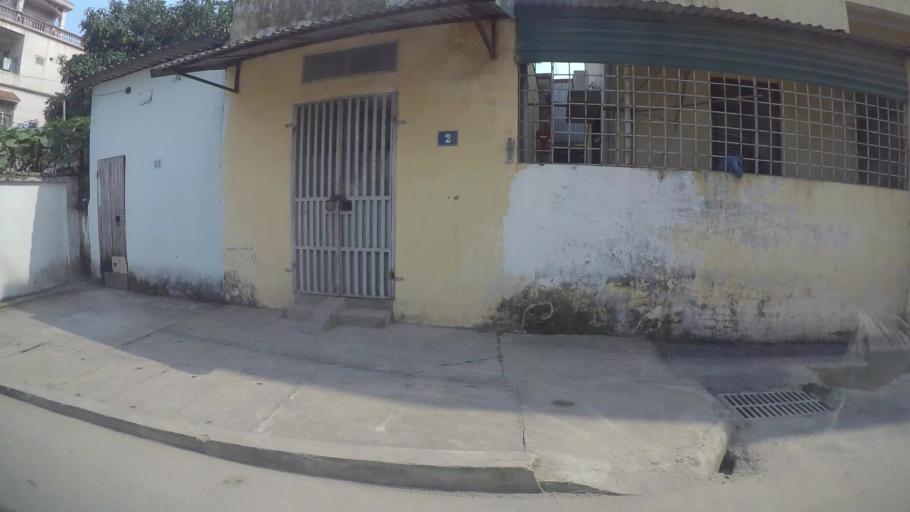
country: VN
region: Ha Noi
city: Ha Dong
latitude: 21.0012
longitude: 105.7531
